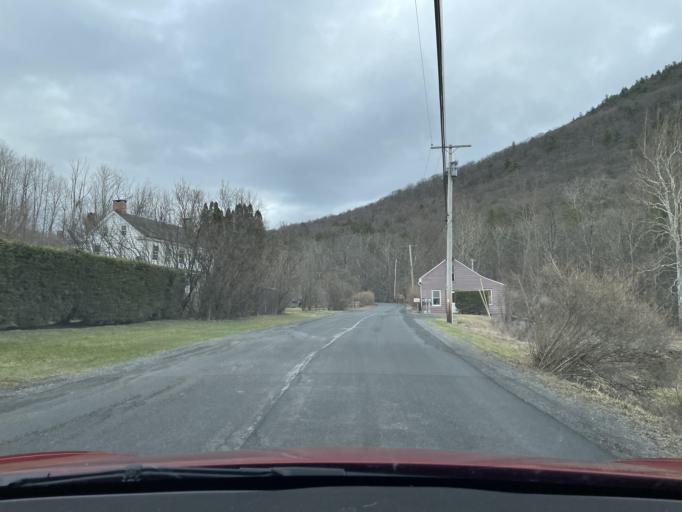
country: US
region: New York
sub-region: Ulster County
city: Woodstock
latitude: 42.0610
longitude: -74.1597
